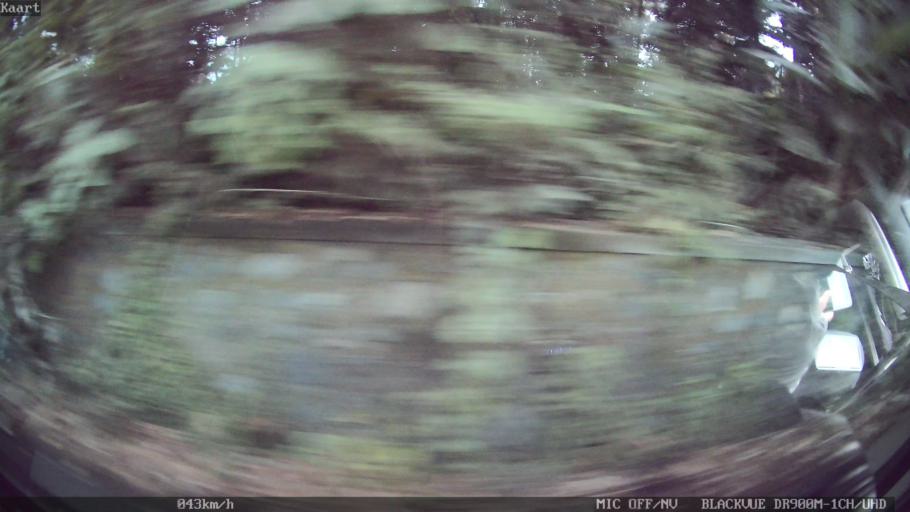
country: ID
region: Bali
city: Banjar Parekan
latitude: -8.5628
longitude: 115.2138
